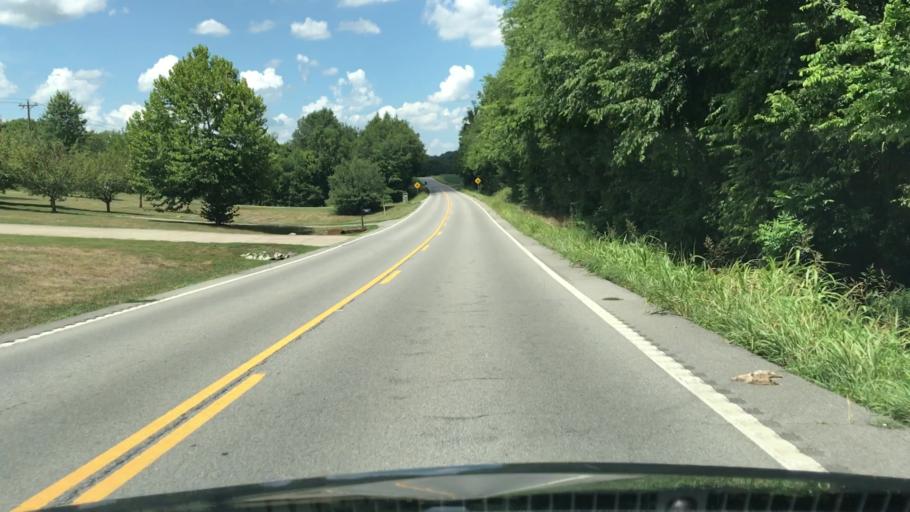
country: US
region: Tennessee
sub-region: Williamson County
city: Nolensville
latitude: 35.8524
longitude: -86.6322
